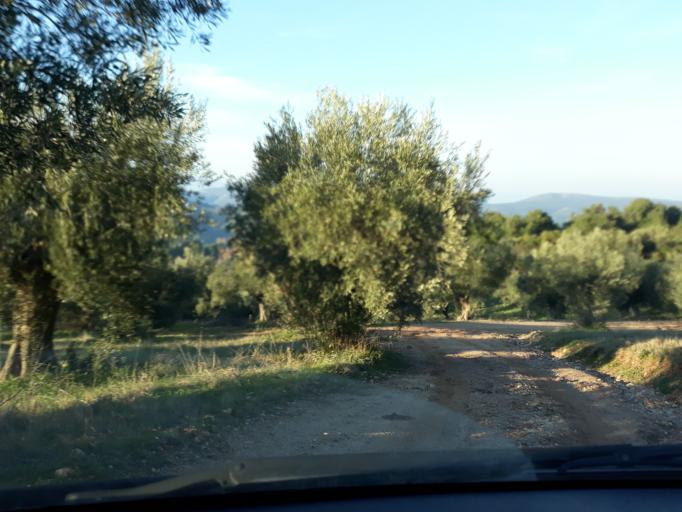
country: GR
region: Central Greece
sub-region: Nomos Voiotias
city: Asopia
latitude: 38.2715
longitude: 23.5323
